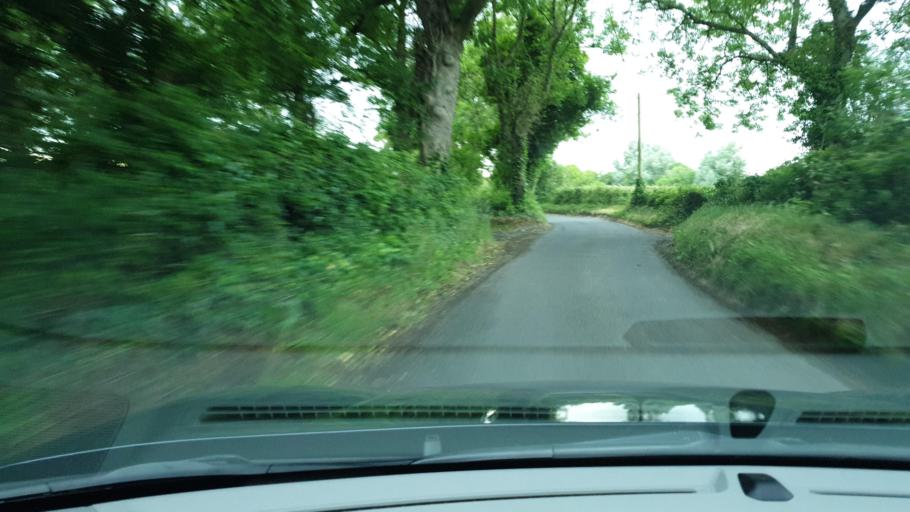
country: IE
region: Leinster
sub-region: An Mhi
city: Navan
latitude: 53.6387
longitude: -6.7184
